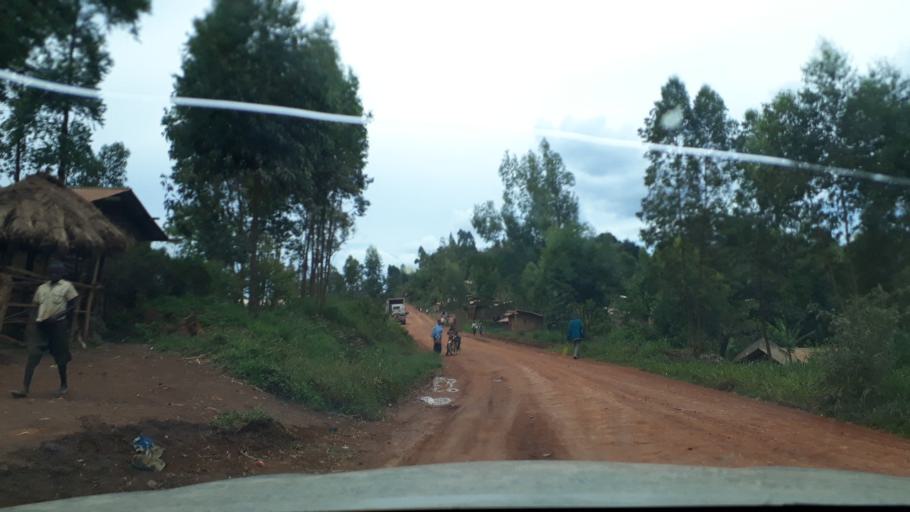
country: CD
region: Eastern Province
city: Bunia
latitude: 1.7562
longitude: 30.3557
